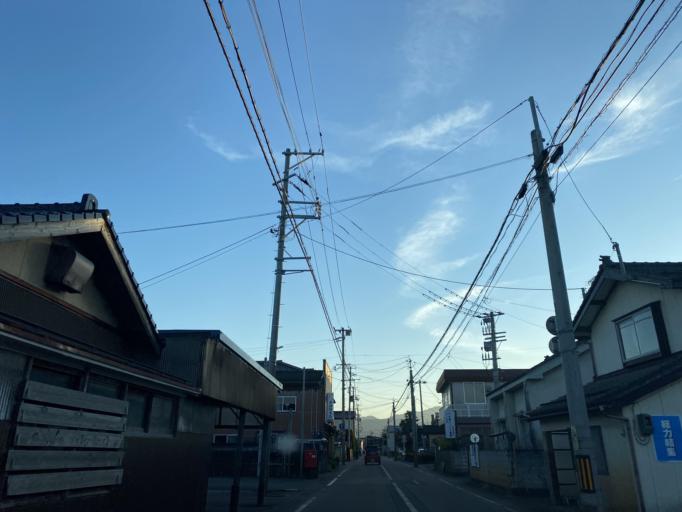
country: JP
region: Niigata
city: Kashiwazaki
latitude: 37.3778
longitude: 138.5657
